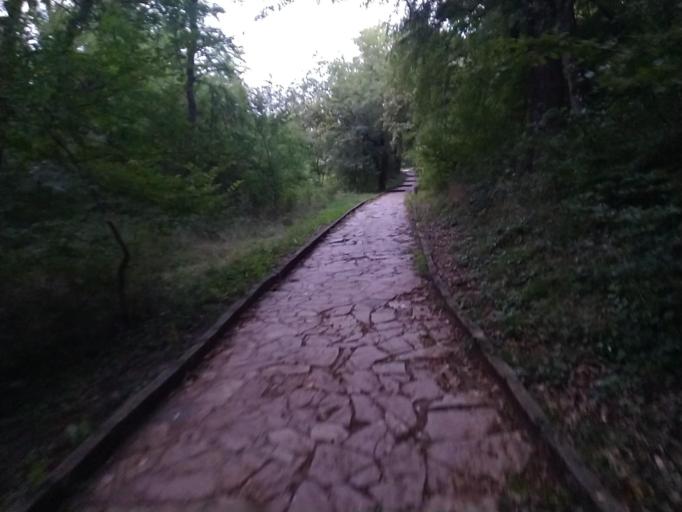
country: BG
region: Plovdiv
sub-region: Obshtina Khisarya
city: Khisarya
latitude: 42.4975
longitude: 24.7036
